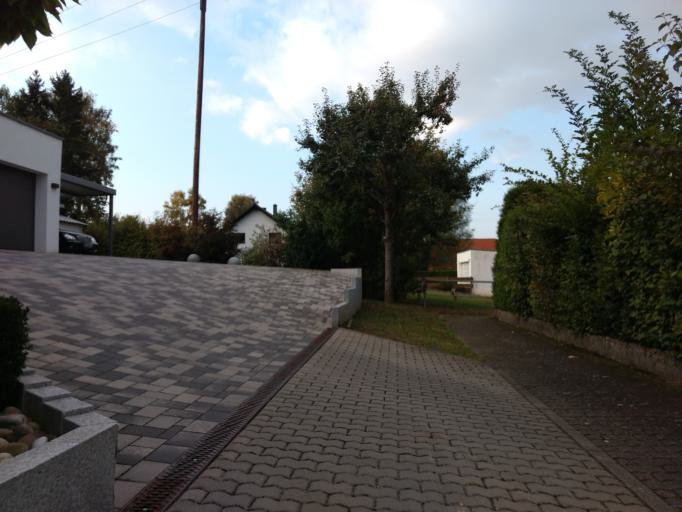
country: DE
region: Saarland
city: Rehlingen-Siersburg
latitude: 49.3737
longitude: 6.6745
